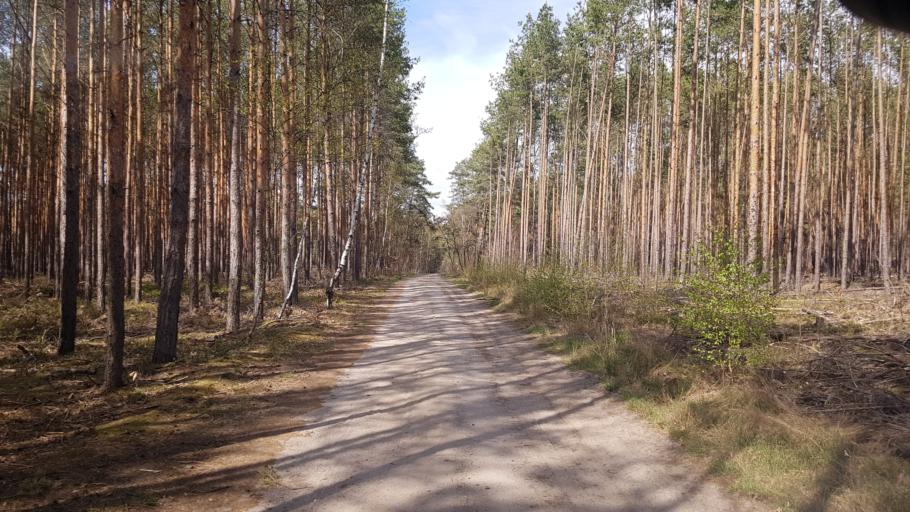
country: DE
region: Brandenburg
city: Ruckersdorf
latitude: 51.5563
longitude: 13.6269
